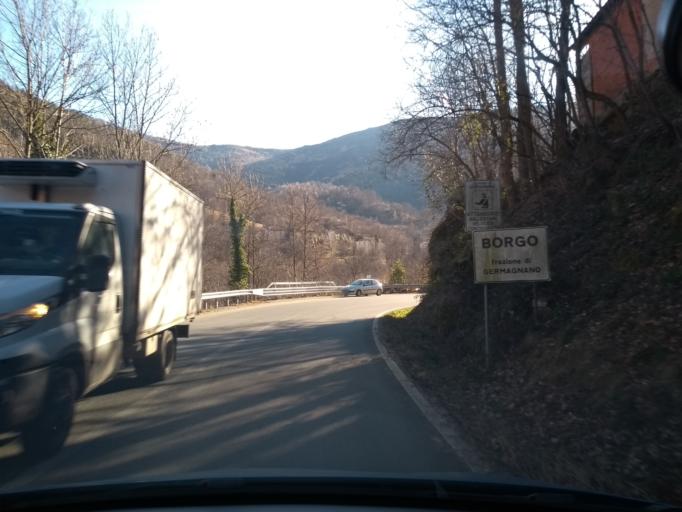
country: IT
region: Piedmont
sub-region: Provincia di Torino
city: La Villa
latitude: 45.2403
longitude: 7.4373
